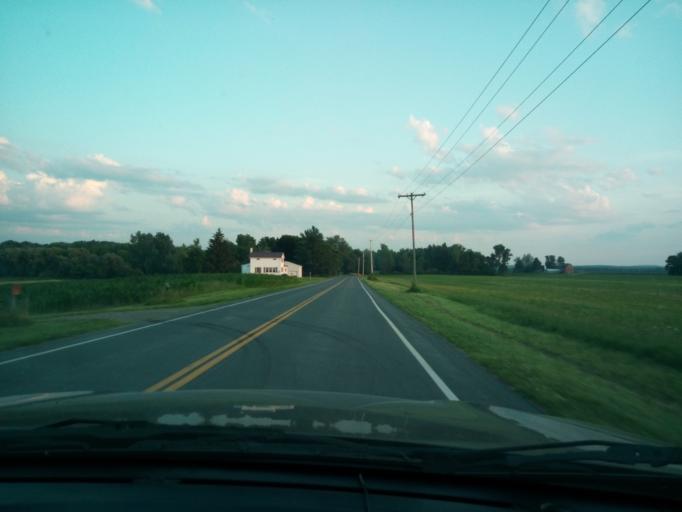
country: US
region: New York
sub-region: Wayne County
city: Clyde
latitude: 43.0332
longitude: -76.7724
